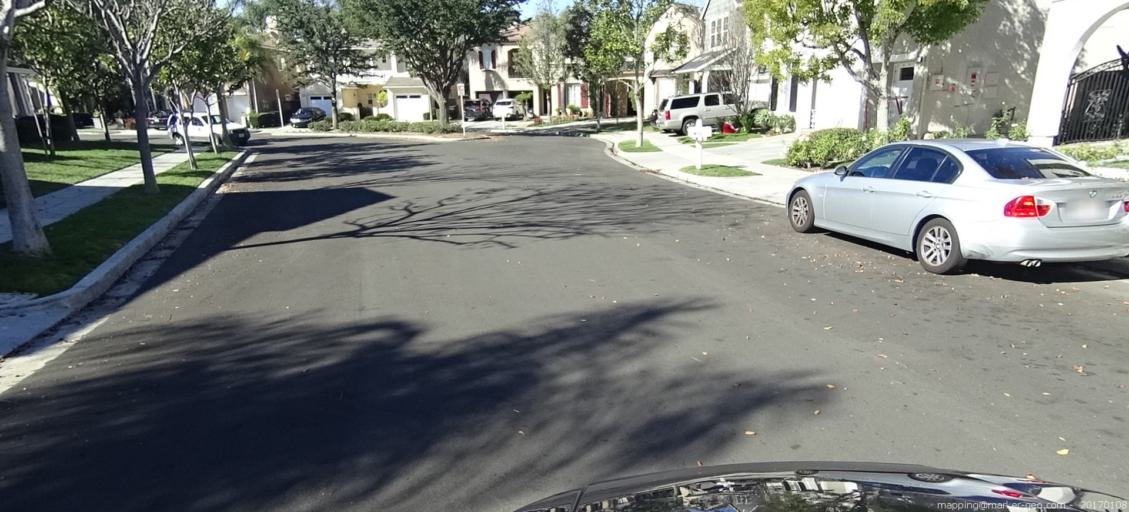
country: US
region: California
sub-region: Orange County
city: Ladera Ranch
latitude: 33.5693
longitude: -117.6392
